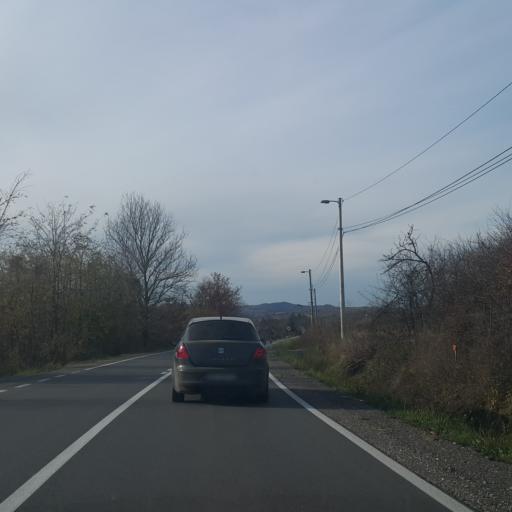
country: RS
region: Central Serbia
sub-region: Sumadijski Okrug
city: Arangelovac
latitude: 44.3373
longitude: 20.4273
